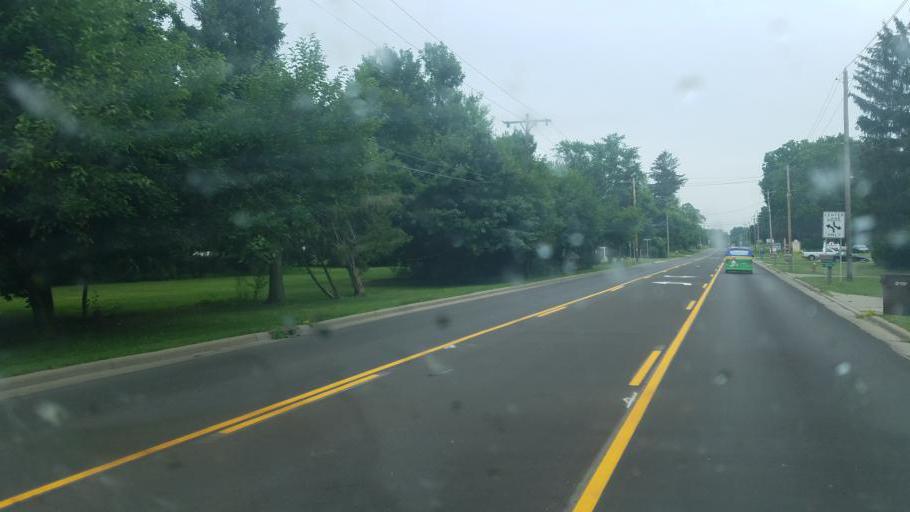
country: US
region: Ohio
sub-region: Summit County
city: Portage Lakes
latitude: 41.0031
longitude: -81.5563
